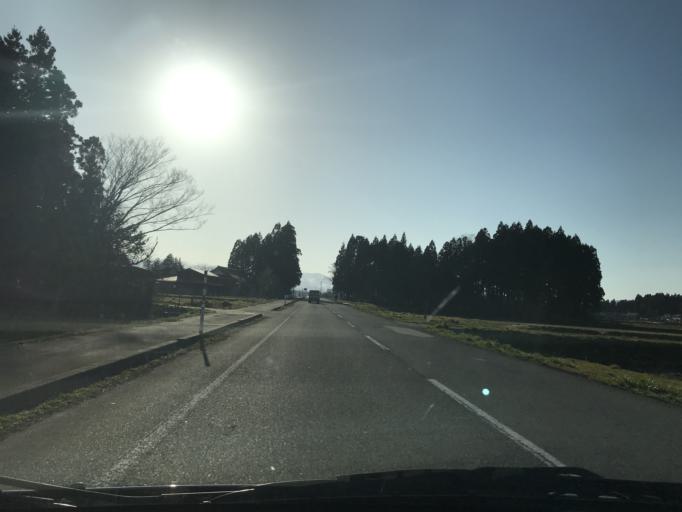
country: JP
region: Iwate
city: Kitakami
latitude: 39.2373
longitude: 141.0719
